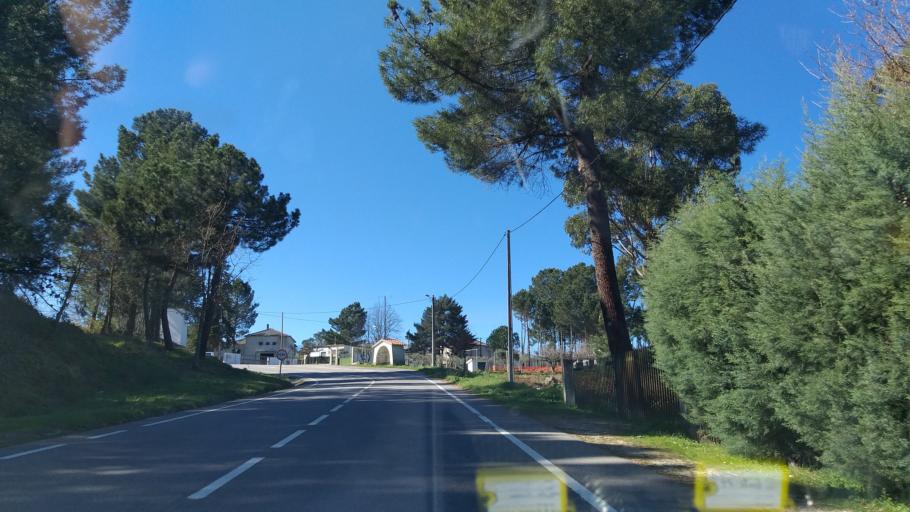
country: PT
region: Guarda
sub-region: Manteigas
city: Manteigas
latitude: 40.5090
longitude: -7.5685
